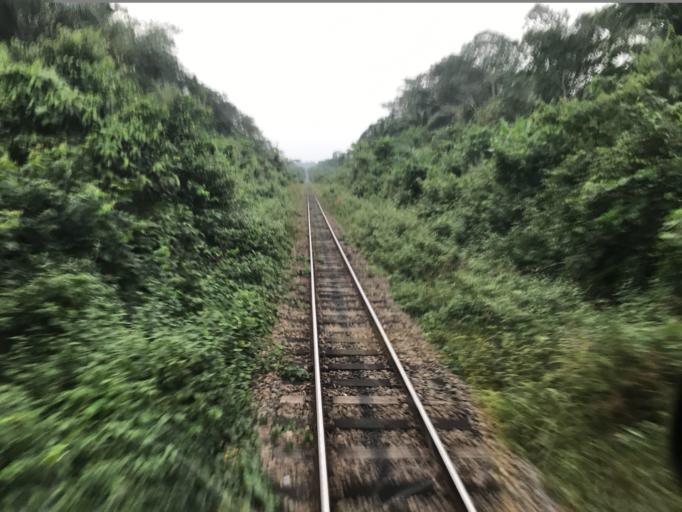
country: CM
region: Littoral
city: Edea
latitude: 3.9765
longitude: 10.0687
